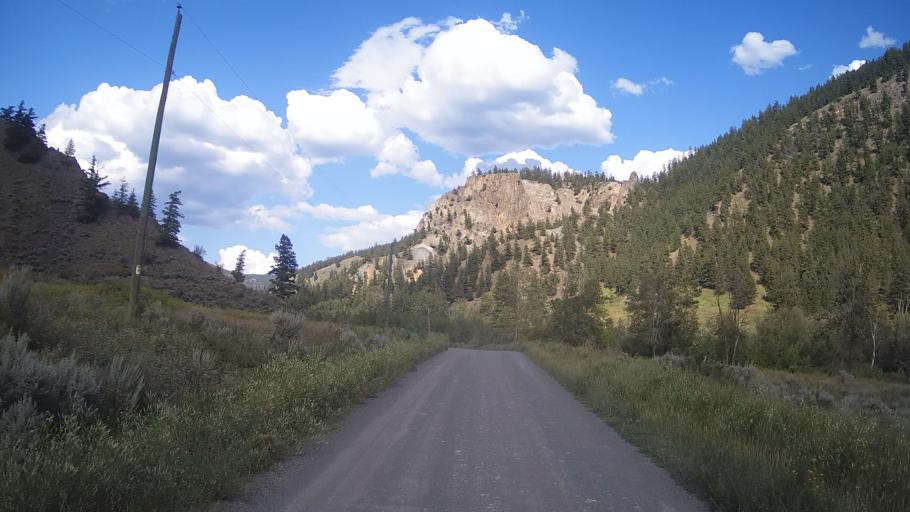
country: CA
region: British Columbia
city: Lillooet
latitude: 51.2263
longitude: -122.0640
